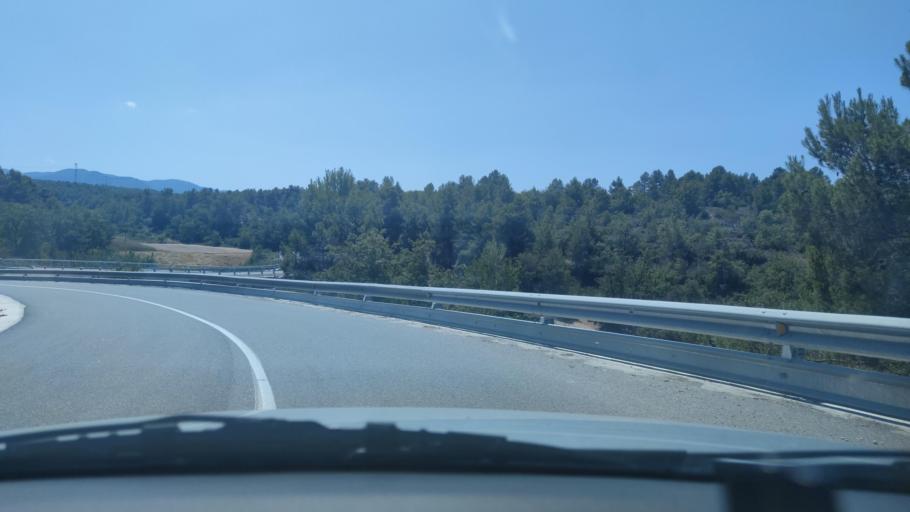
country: ES
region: Catalonia
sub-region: Provincia de Lleida
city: Vinaixa
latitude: 41.4139
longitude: 0.9560
